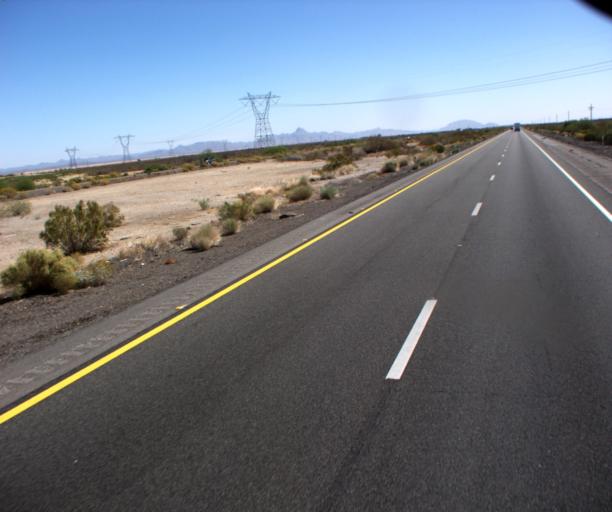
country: US
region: Arizona
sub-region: La Paz County
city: Salome
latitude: 33.5759
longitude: -113.4006
